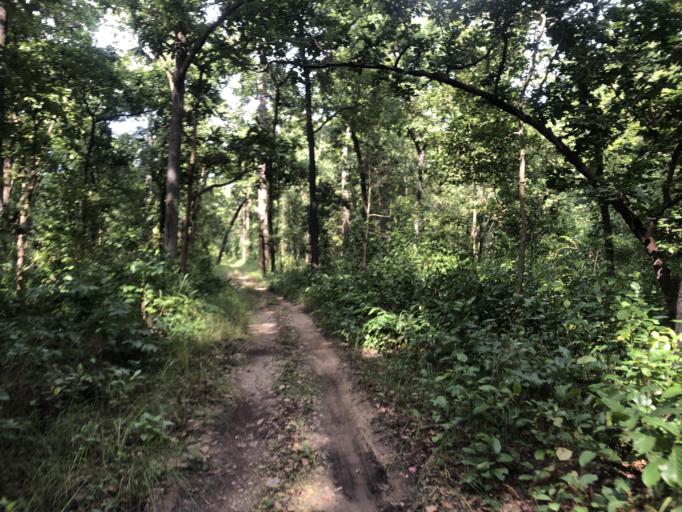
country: NP
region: Far Western
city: Tikapur
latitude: 28.5372
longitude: 81.2849
